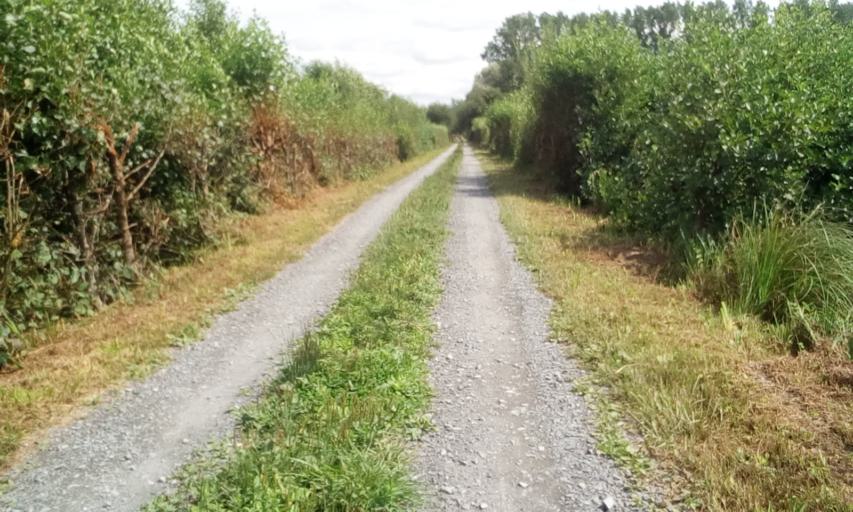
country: FR
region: Lower Normandy
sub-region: Departement du Calvados
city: Bavent
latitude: 49.2391
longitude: -0.1662
